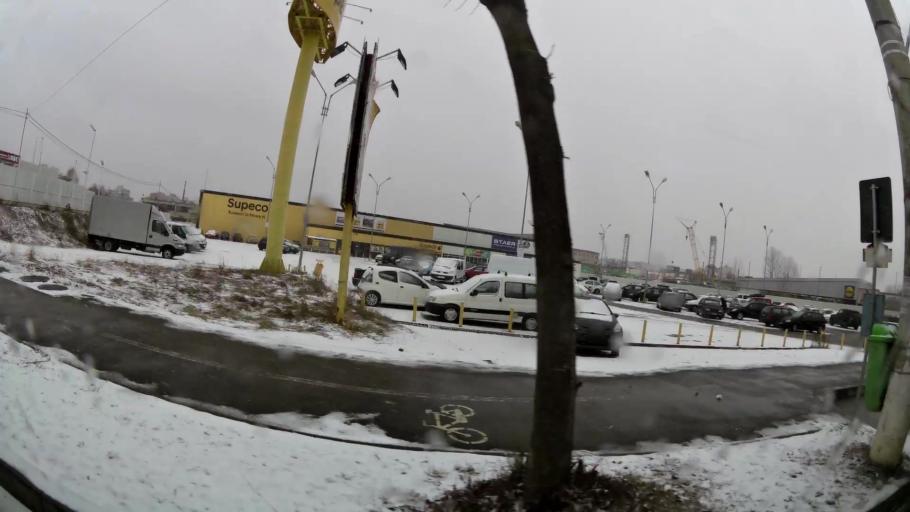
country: RO
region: Dambovita
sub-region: Municipiul Targoviste
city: Targoviste
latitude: 44.9194
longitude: 25.4593
